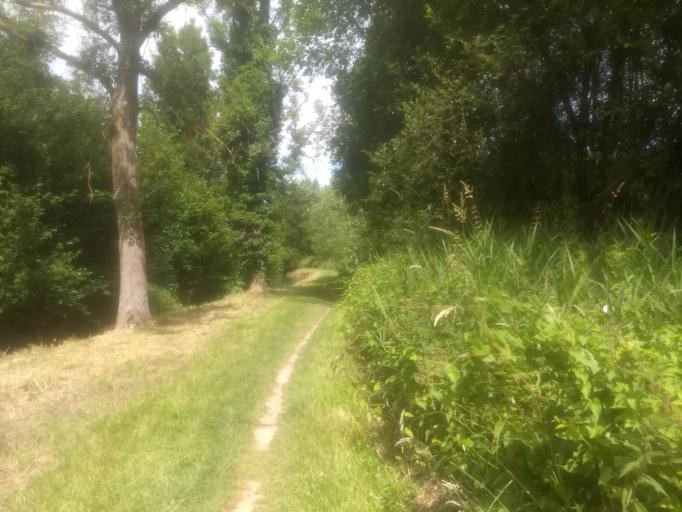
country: FR
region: Nord-Pas-de-Calais
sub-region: Departement du Pas-de-Calais
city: Maroeuil
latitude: 50.3156
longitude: 2.7093
